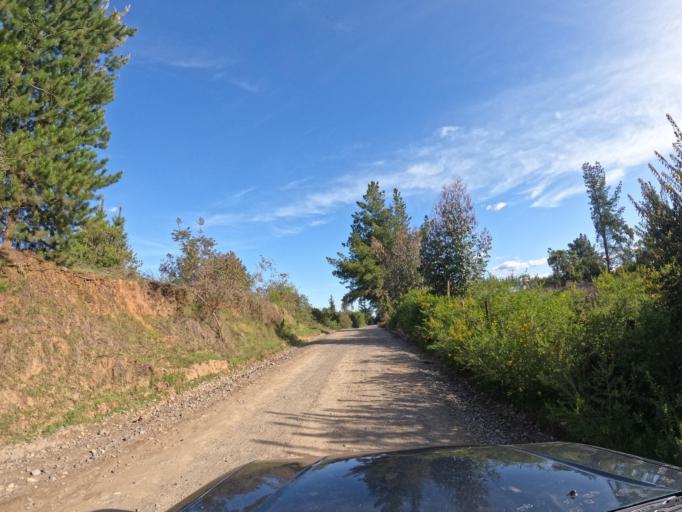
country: CL
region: Biobio
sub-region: Provincia de Biobio
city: La Laja
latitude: -37.1537
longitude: -72.7261
